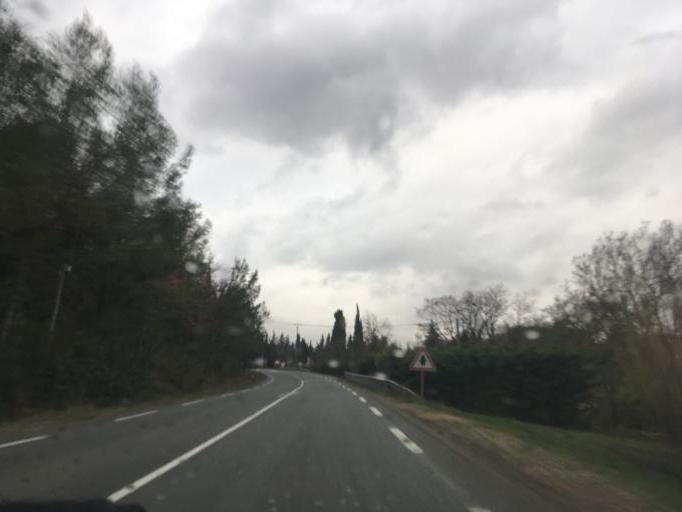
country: FR
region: Provence-Alpes-Cote d'Azur
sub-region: Departement du Var
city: Sainte-Anastasie-sur-Issole
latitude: 43.3394
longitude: 6.1243
